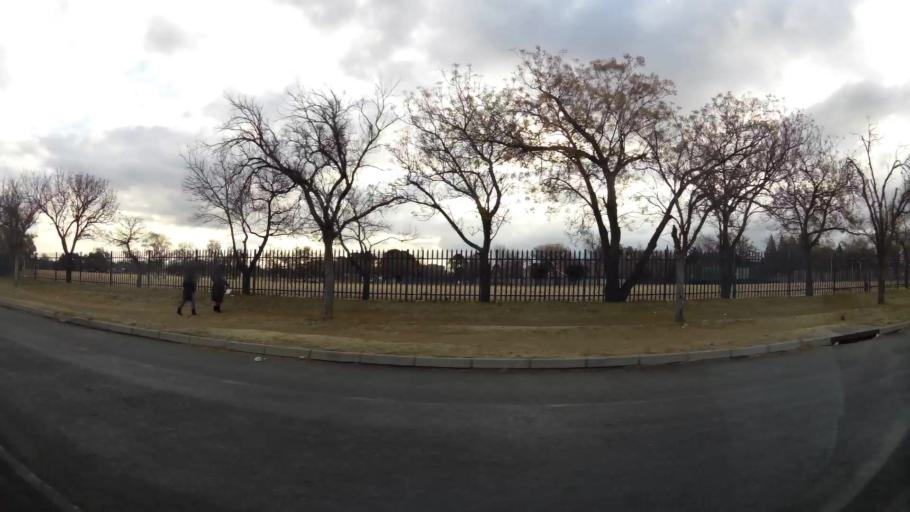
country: ZA
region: Orange Free State
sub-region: Lejweleputswa District Municipality
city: Welkom
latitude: -27.9800
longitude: 26.7312
